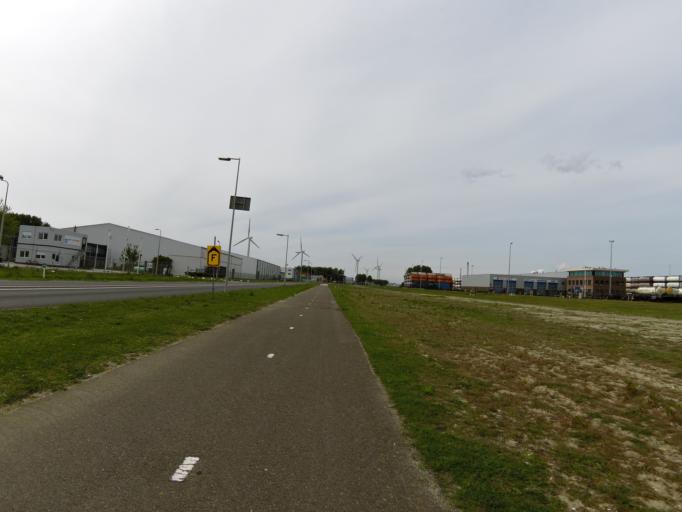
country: NL
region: South Holland
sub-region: Gemeente Brielle
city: Brielle
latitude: 51.9184
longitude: 4.1846
